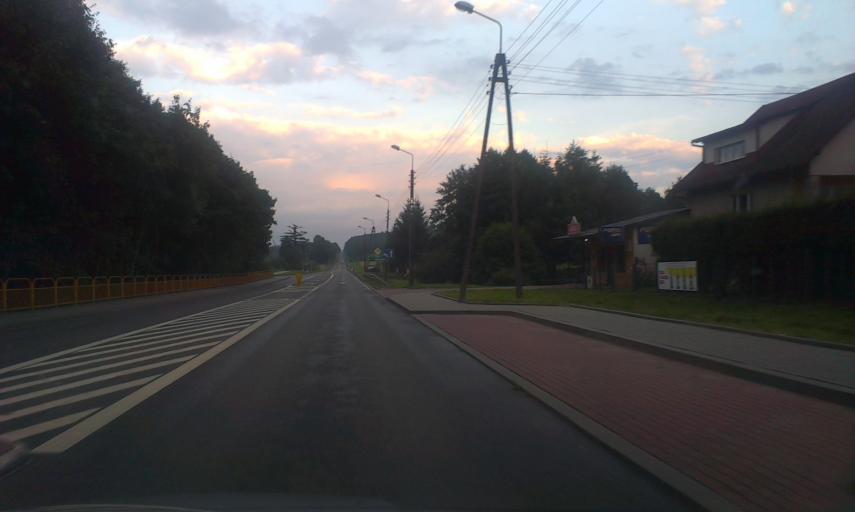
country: PL
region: West Pomeranian Voivodeship
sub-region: Powiat koszalinski
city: Sianow
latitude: 54.1242
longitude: 16.3039
